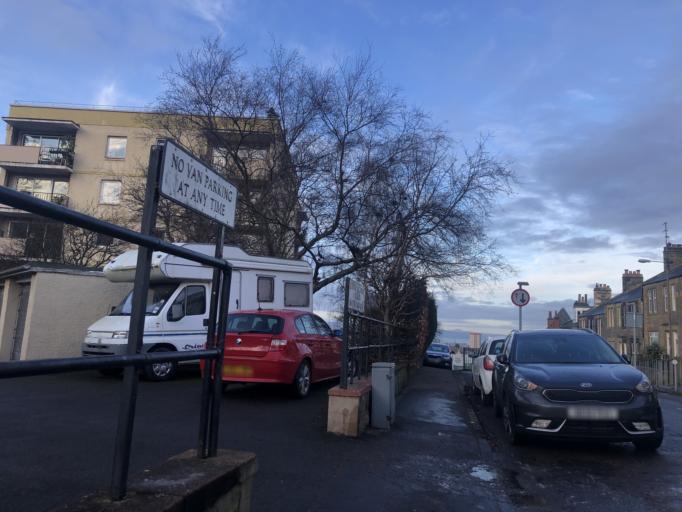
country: GB
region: Scotland
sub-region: West Lothian
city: Seafield
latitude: 55.9531
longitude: -3.1521
